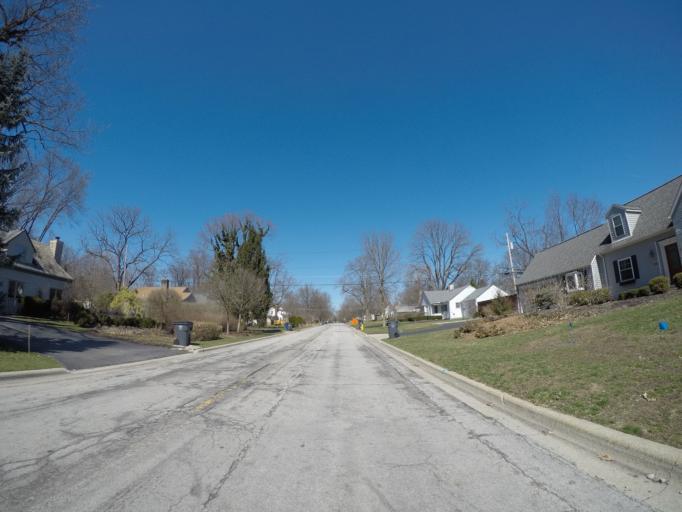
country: US
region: Ohio
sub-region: Franklin County
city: Upper Arlington
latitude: 40.0136
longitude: -83.0727
